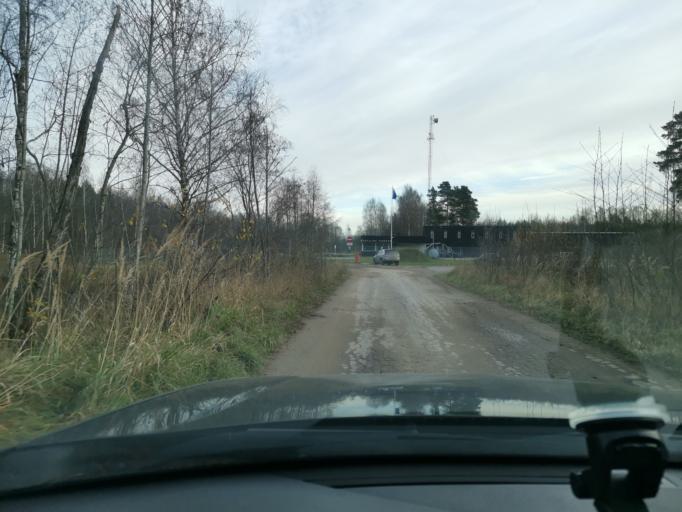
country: EE
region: Ida-Virumaa
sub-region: Sillamaee linn
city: Sillamae
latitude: 59.2582
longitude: 27.9144
